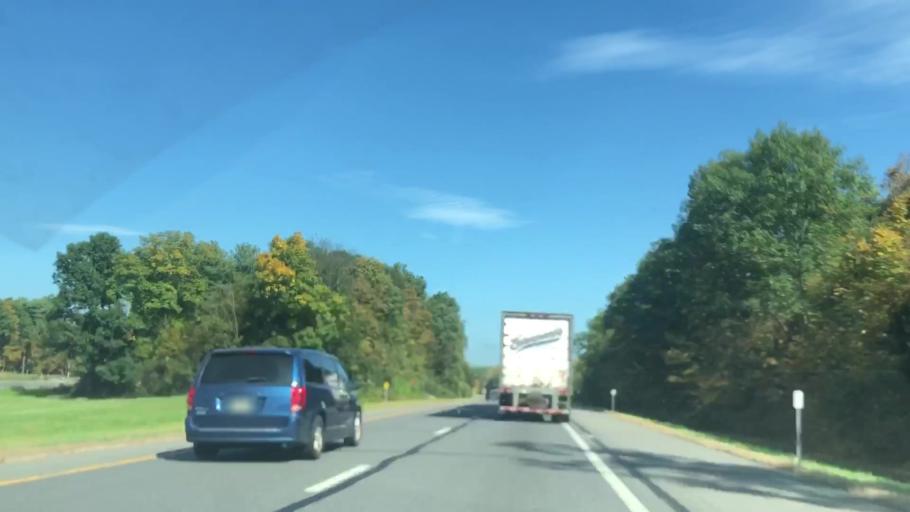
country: US
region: New York
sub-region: Greene County
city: Coxsackie
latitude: 42.3333
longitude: -73.8601
